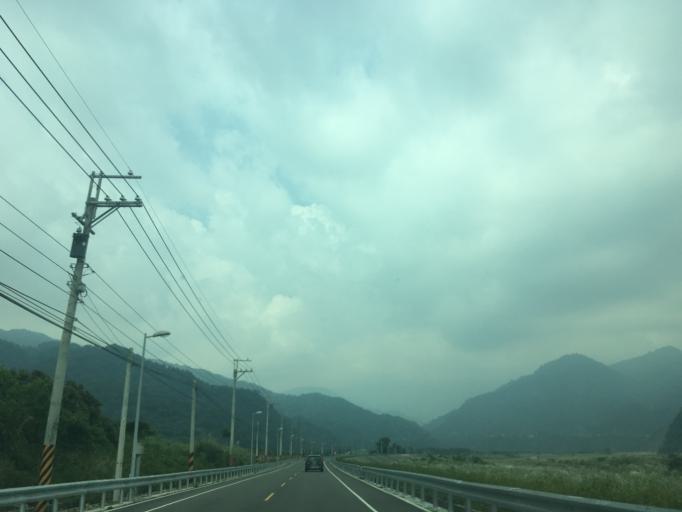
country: TW
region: Taiwan
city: Fengyuan
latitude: 24.2963
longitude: 120.8799
